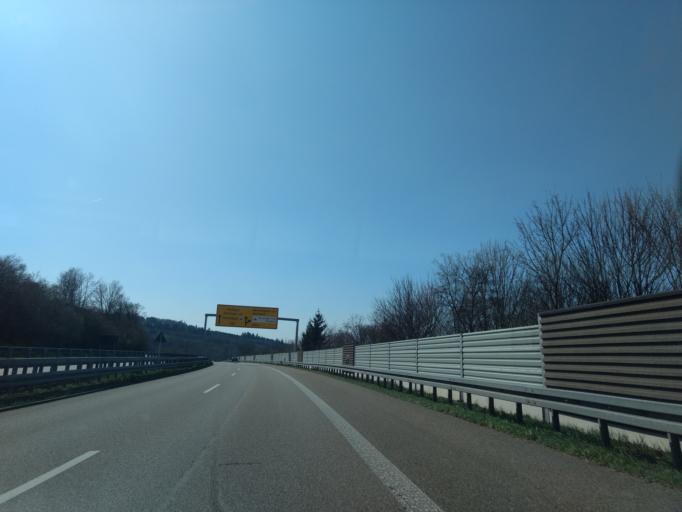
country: DE
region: Baden-Wuerttemberg
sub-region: Regierungsbezirk Stuttgart
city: Reichenbach an der Fils
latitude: 48.7066
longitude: 9.4565
